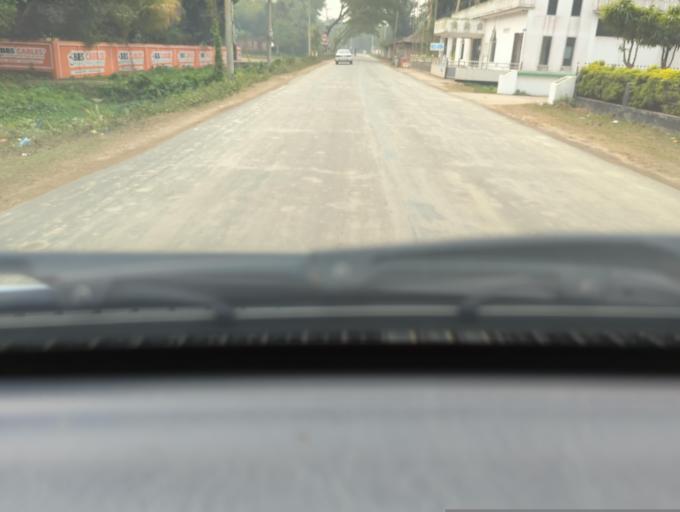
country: BD
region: Sylhet
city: Maulavi Bazar
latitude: 24.5202
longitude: 91.7305
